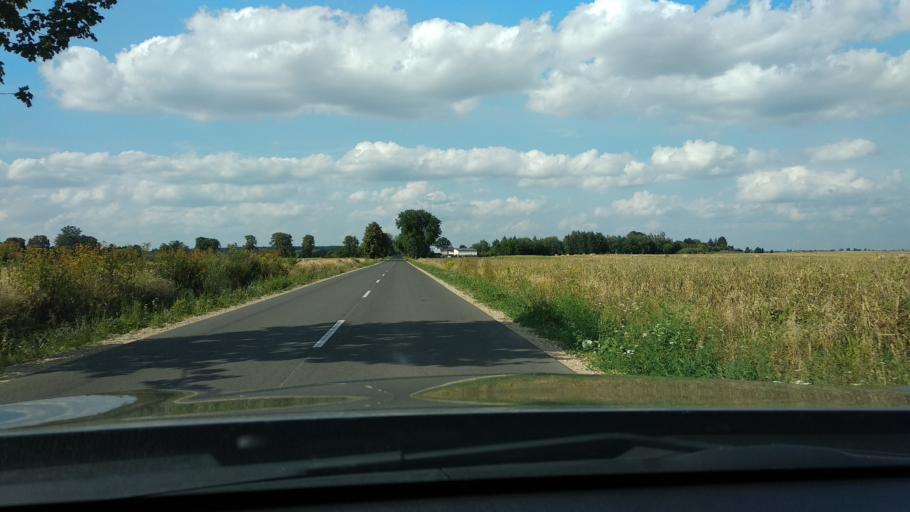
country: PL
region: Masovian Voivodeship
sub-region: Powiat pultuski
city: Zatory
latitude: 52.5553
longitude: 21.1877
